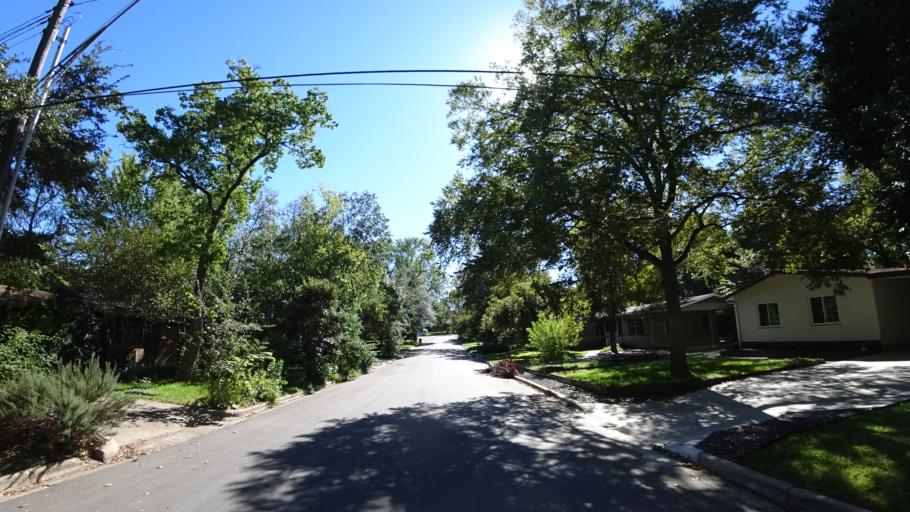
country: US
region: Texas
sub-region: Travis County
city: Austin
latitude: 30.3214
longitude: -97.7519
